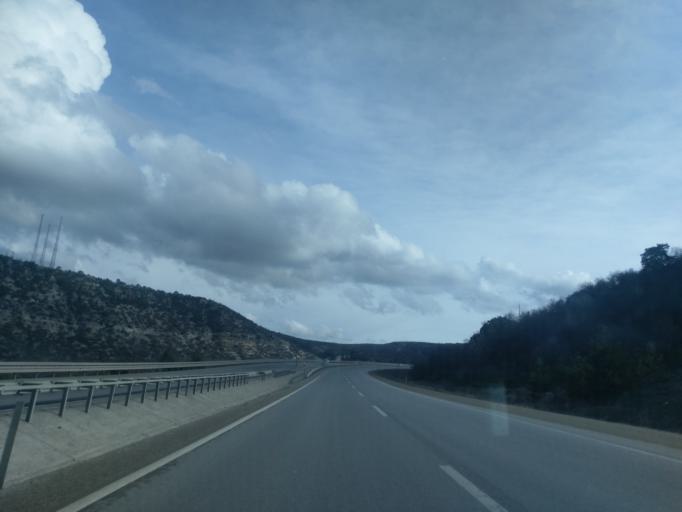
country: TR
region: Kuetahya
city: Sabuncu
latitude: 39.5637
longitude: 30.0738
